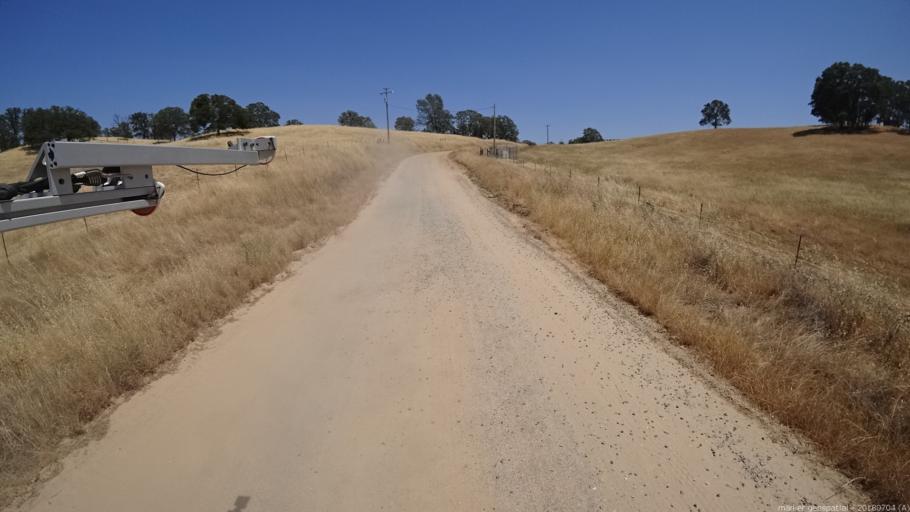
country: US
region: California
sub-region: Madera County
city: Yosemite Lakes
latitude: 37.1436
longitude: -119.6749
